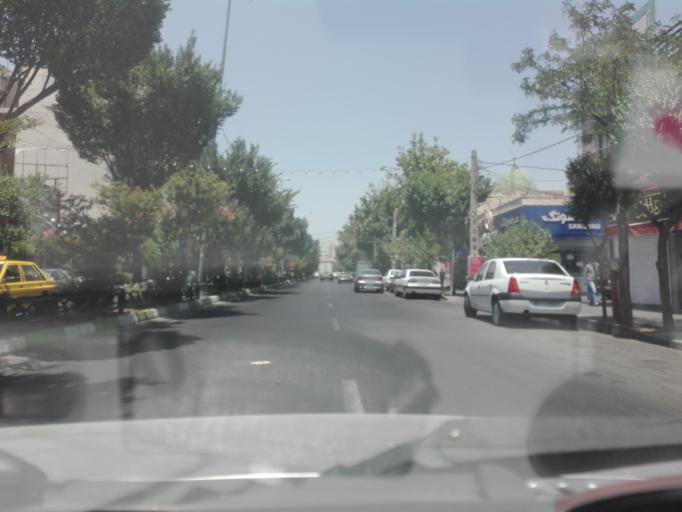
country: IR
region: Tehran
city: Shahre Jadide Andisheh
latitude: 35.7341
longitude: 50.9910
